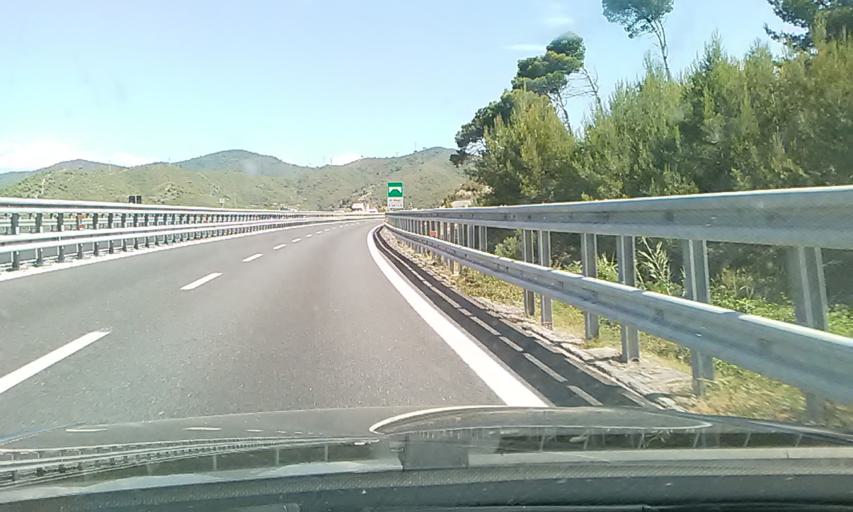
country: IT
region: Liguria
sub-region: Provincia di Savona
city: Laigueglia
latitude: 43.9845
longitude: 8.1364
